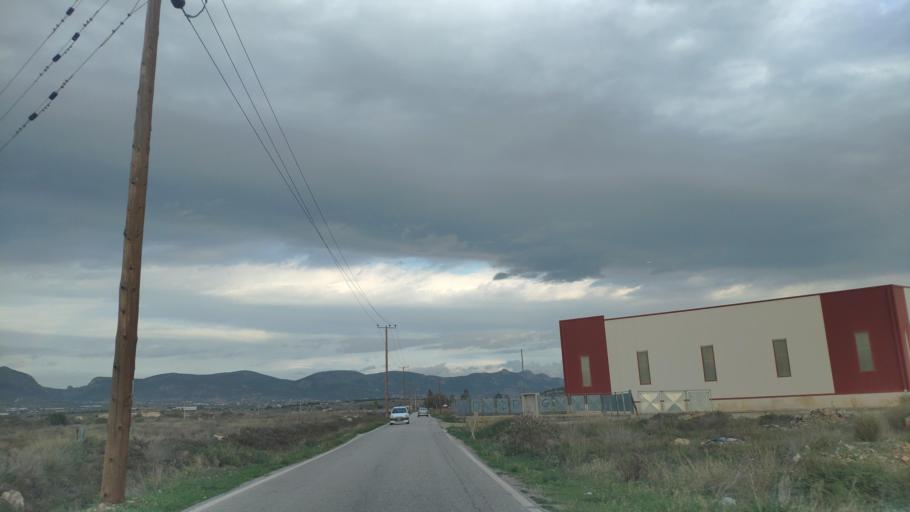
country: GR
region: Attica
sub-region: Nomarchia Dytikis Attikis
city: Megara
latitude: 37.9833
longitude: 23.3855
